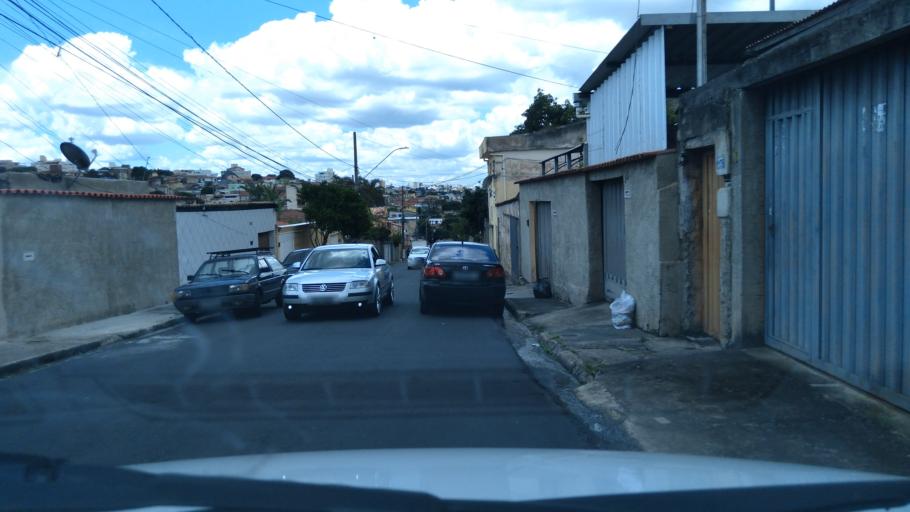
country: BR
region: Minas Gerais
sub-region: Belo Horizonte
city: Belo Horizonte
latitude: -19.9133
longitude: -43.8989
